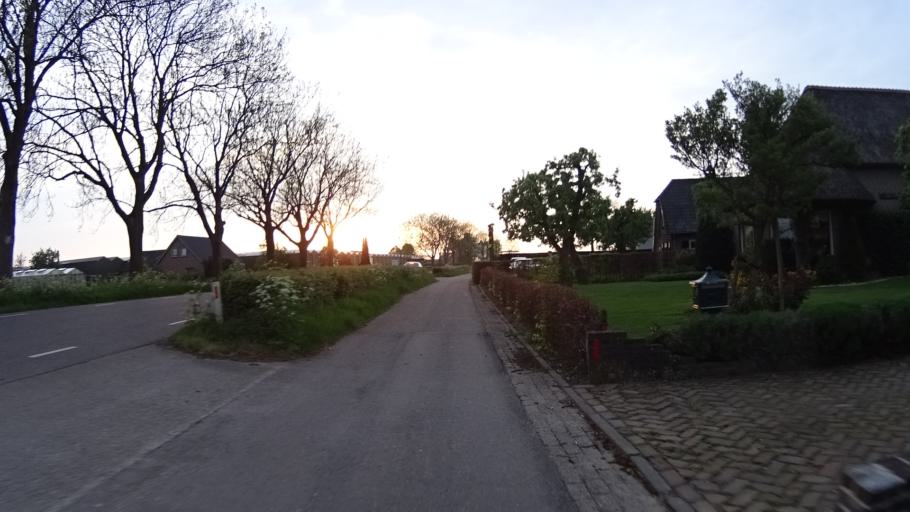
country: NL
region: North Brabant
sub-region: Gemeente Woudrichem
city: Woudrichem
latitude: 51.8007
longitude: 5.0099
